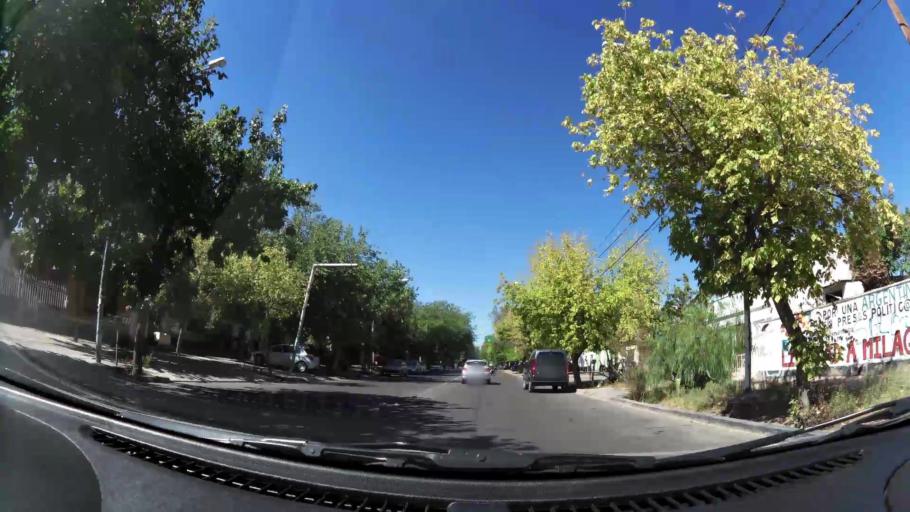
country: AR
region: Mendoza
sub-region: Departamento de Godoy Cruz
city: Godoy Cruz
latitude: -32.9138
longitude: -68.8598
